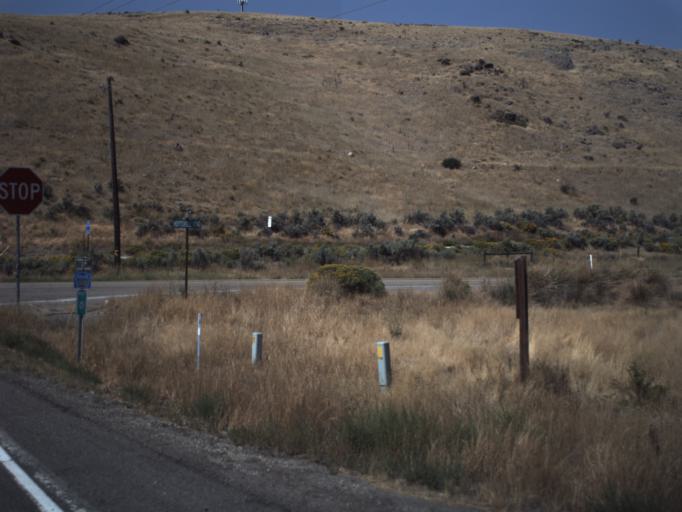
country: US
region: Utah
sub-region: Summit County
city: Coalville
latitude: 40.8132
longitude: -111.4037
